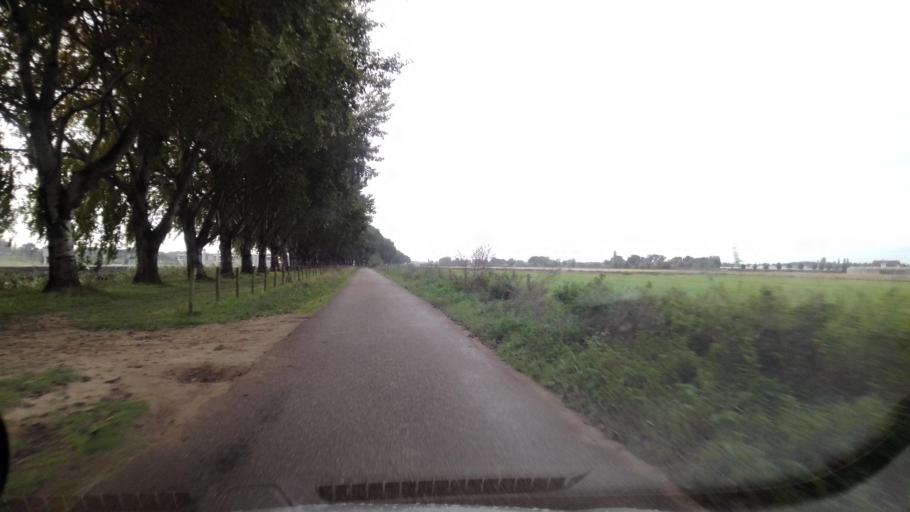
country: NL
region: Limburg
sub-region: Gemeente Venlo
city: Tegelen
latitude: 51.3260
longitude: 6.1135
